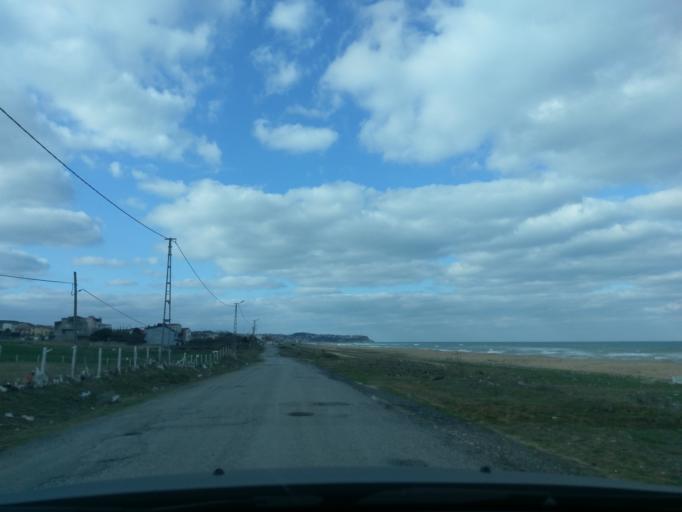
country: TR
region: Istanbul
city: Durusu
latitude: 41.3249
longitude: 28.7269
